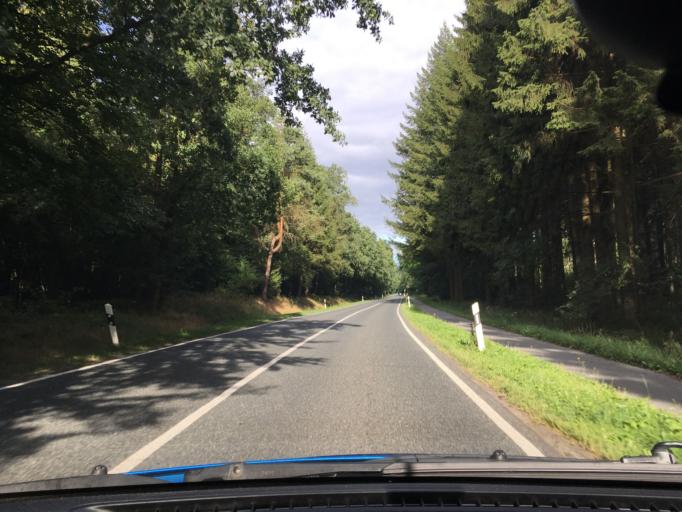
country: DE
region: Lower Saxony
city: Neu Wulmstorf
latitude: 53.4060
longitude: 9.8392
